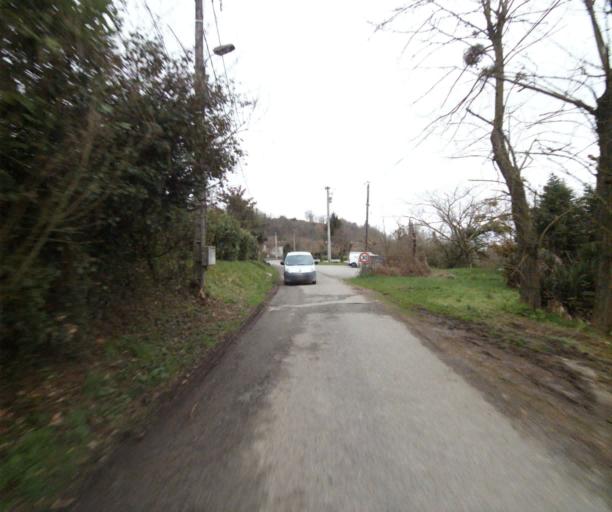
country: FR
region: Midi-Pyrenees
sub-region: Departement de l'Ariege
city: Saverdun
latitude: 43.2276
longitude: 1.5815
